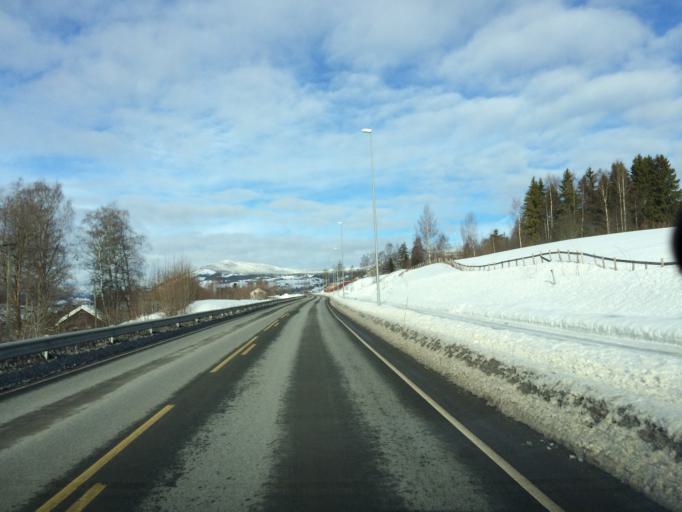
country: NO
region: Oppland
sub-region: Gausdal
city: Segalstad bru
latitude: 61.1931
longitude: 10.3140
